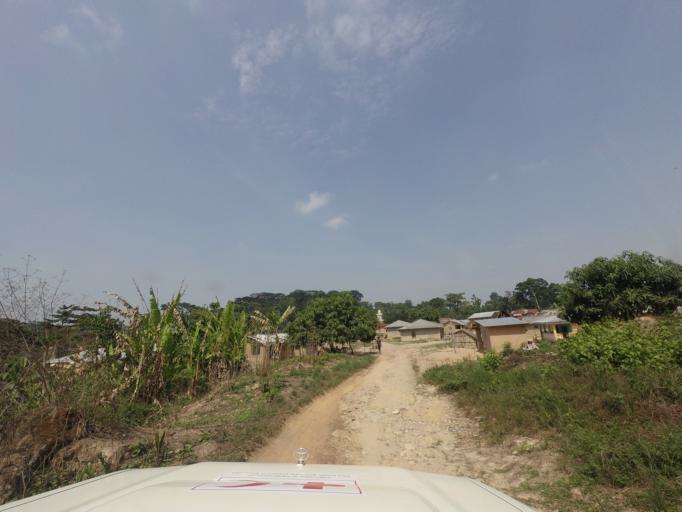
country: LR
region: Lofa
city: Voinjama
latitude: 8.5161
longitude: -9.6274
